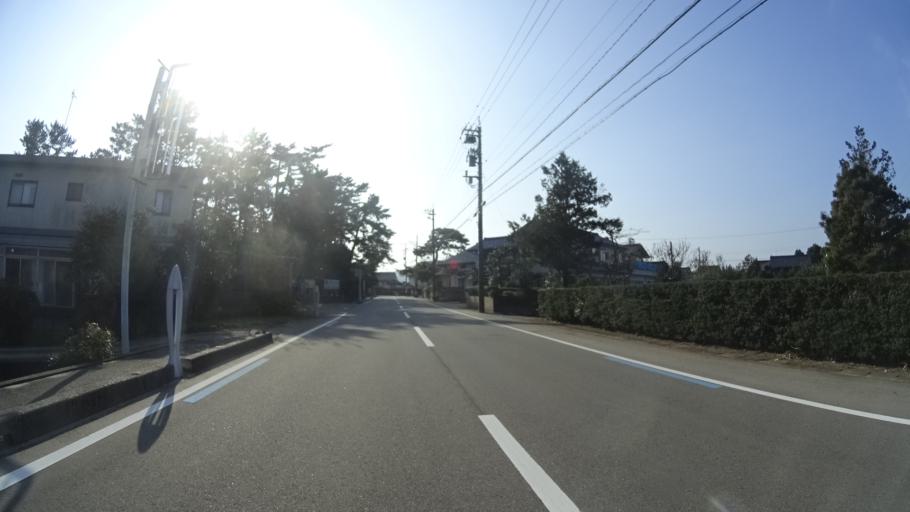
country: JP
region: Toyama
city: Himi
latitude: 36.8307
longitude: 137.0126
